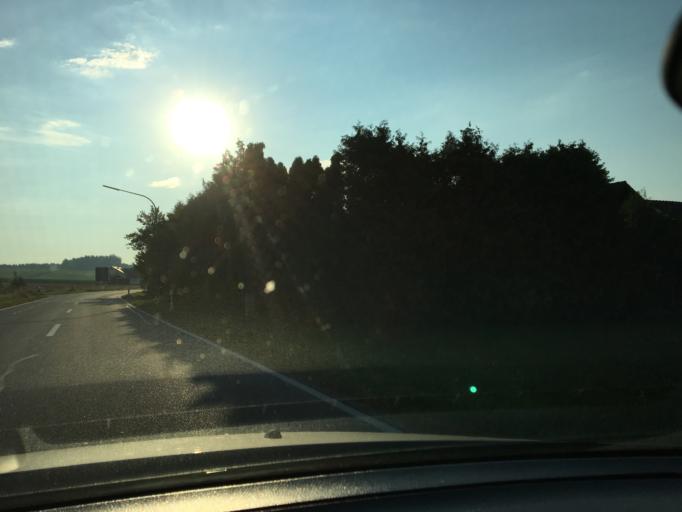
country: DE
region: Bavaria
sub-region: Lower Bavaria
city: Vilsbiburg
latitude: 48.4994
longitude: 12.3514
